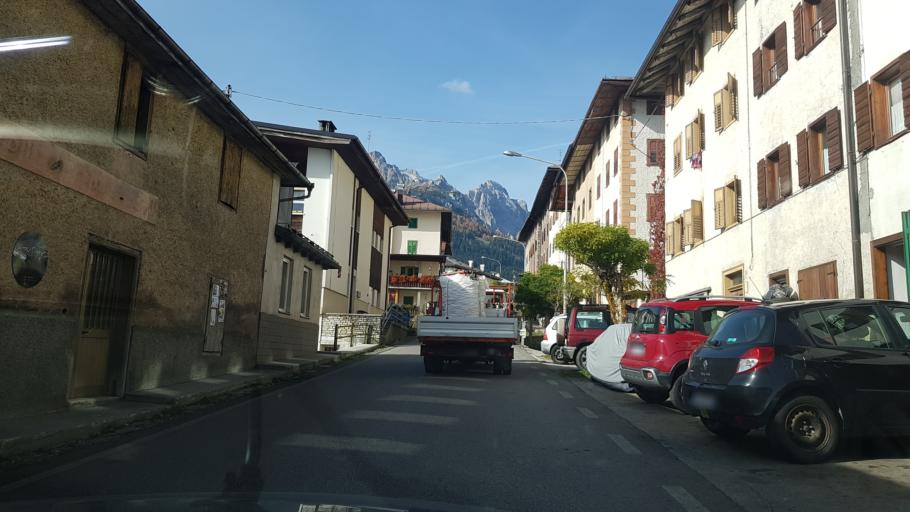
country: IT
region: Veneto
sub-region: Provincia di Belluno
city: Candide
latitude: 46.5993
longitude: 12.4939
